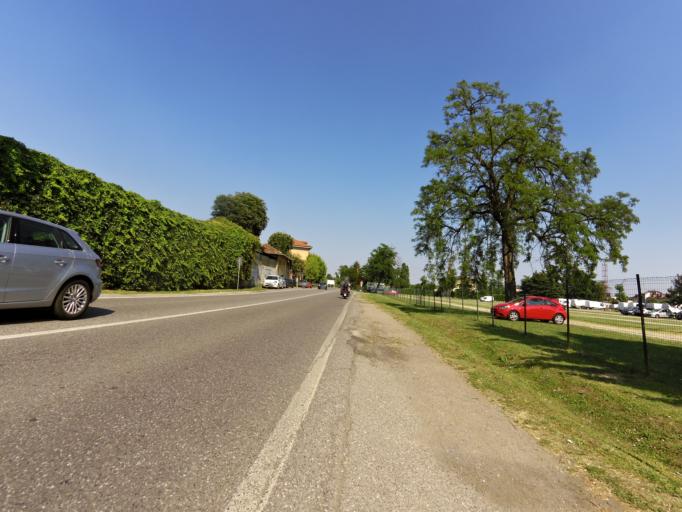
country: IT
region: Lombardy
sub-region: Citta metropolitana di Milano
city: Novegro-Tregarezzo-San Felice
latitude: 45.4726
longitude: 9.2753
